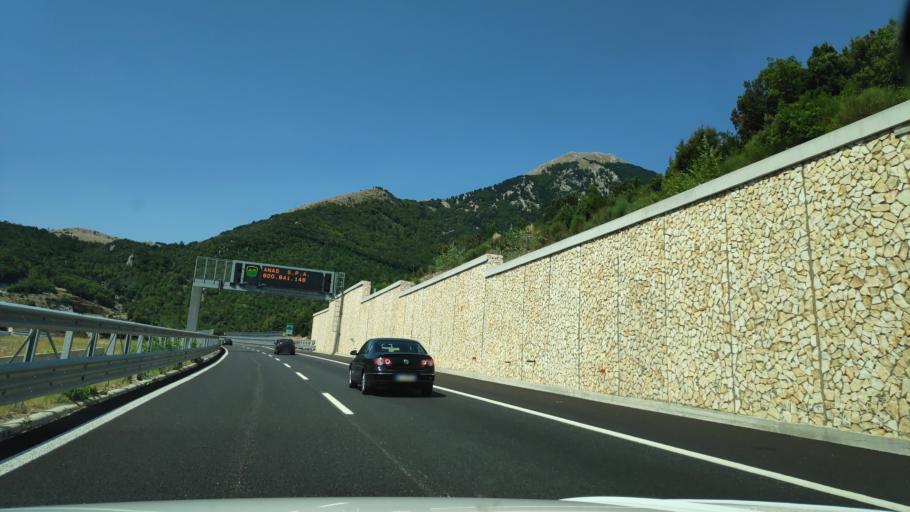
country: IT
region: Calabria
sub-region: Provincia di Cosenza
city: Morano Calabro
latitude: 39.8899
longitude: 16.1457
